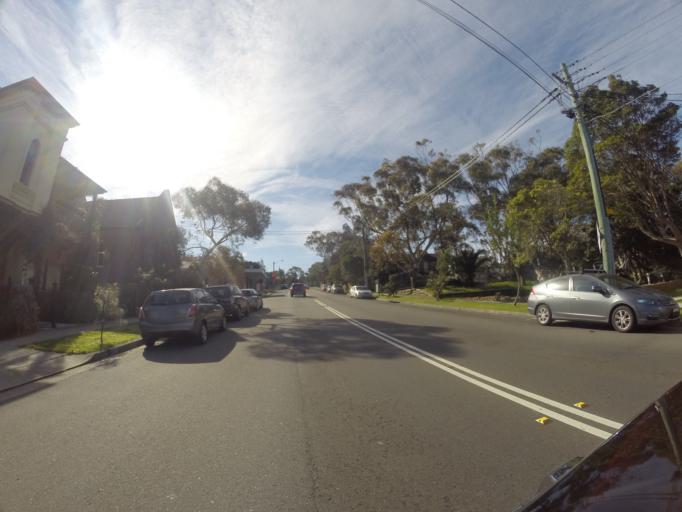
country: AU
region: New South Wales
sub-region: Randwick
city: Clovelly
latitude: -33.9083
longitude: 151.2595
